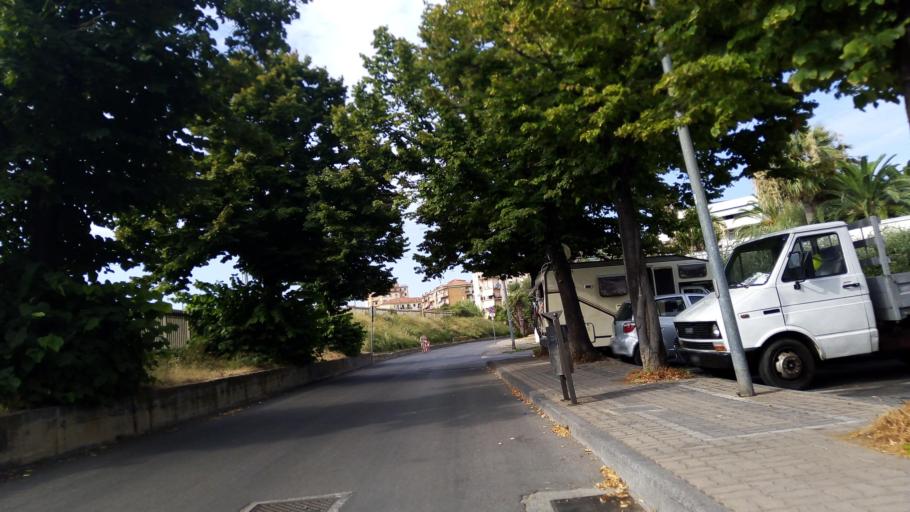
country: IT
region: Liguria
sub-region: Provincia di Savona
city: Albenga
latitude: 44.0506
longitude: 8.2236
